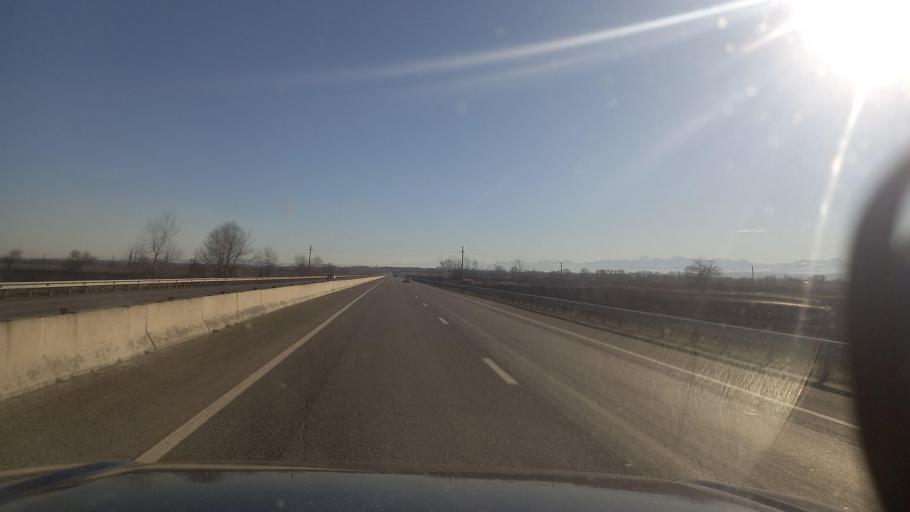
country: RU
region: Kabardino-Balkariya
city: Nartan
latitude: 43.5806
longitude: 43.6954
